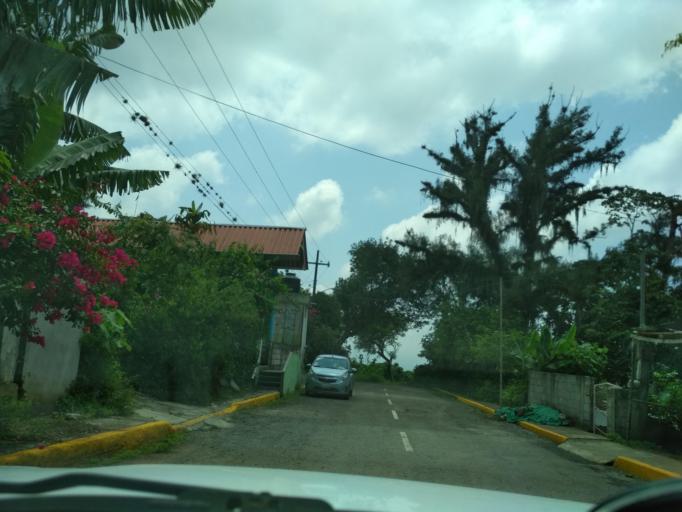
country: MX
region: Veracruz
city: Ixtac Zoquitlan
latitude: 18.8766
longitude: -97.0762
